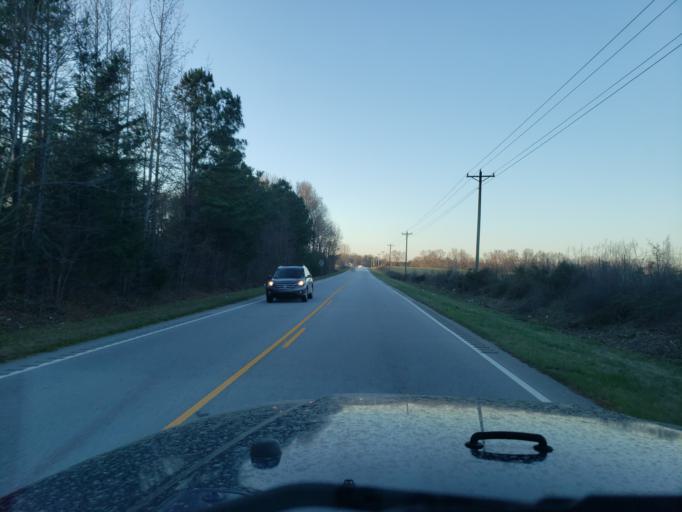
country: US
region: South Carolina
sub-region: York County
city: Clover
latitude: 35.1259
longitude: -81.3079
